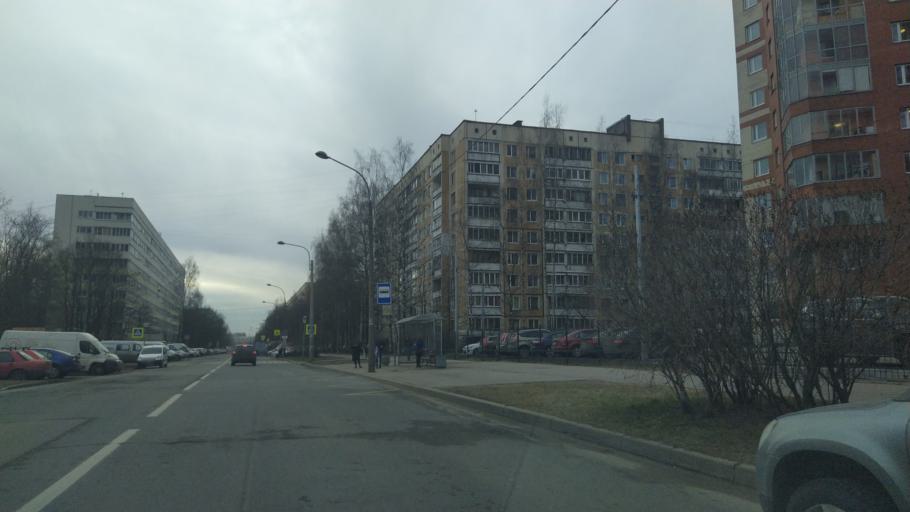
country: RU
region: St.-Petersburg
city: Grazhdanka
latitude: 60.0307
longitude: 30.4270
